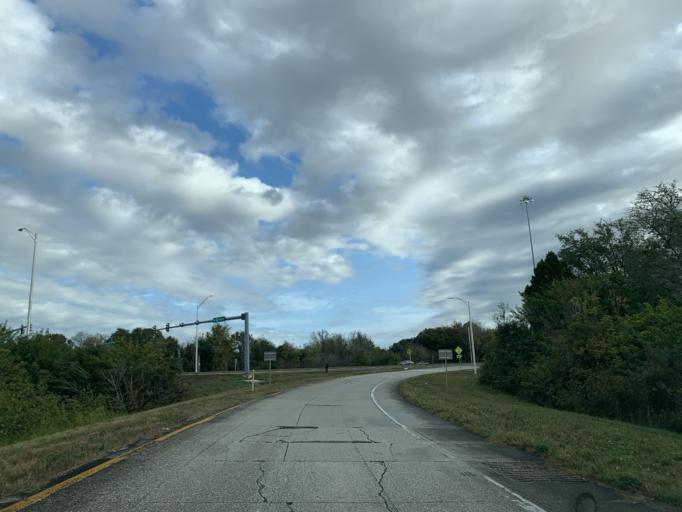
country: US
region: Florida
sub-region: Hillsborough County
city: Mango
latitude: 27.9806
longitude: -82.3236
